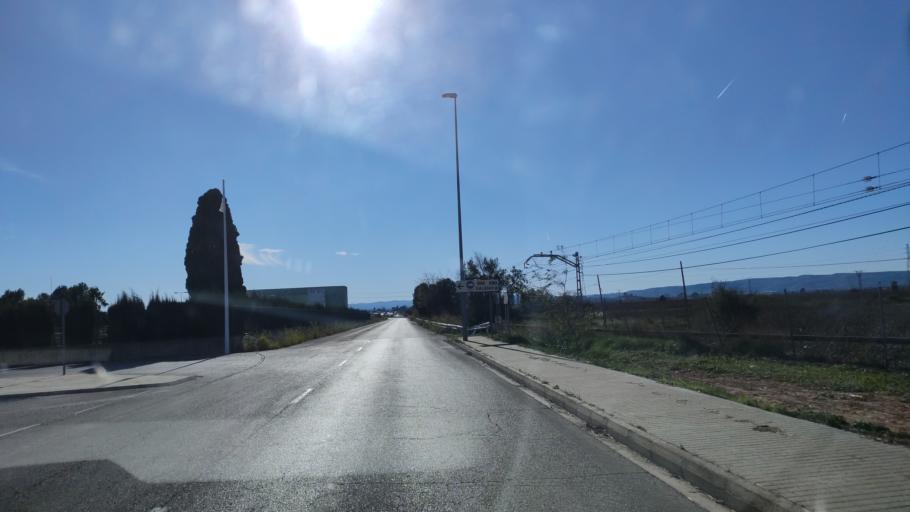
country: ES
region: Valencia
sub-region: Provincia de Valencia
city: L'Alcudia
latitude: 39.1860
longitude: -0.5111
